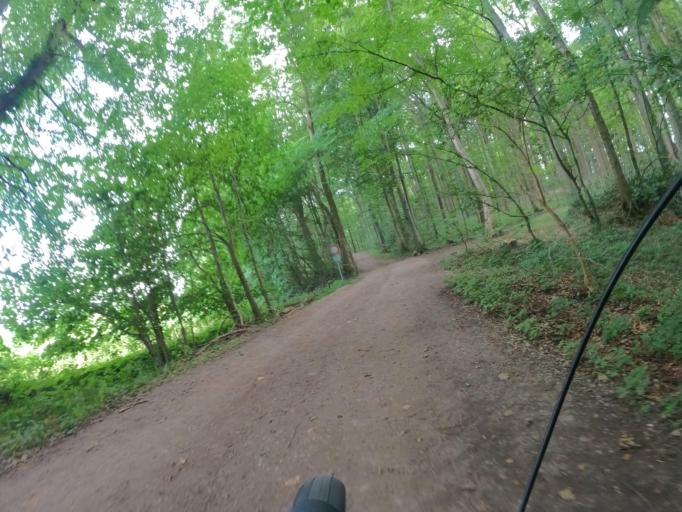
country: DE
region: Schleswig-Holstein
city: Steinberg
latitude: 54.7901
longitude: 9.7871
